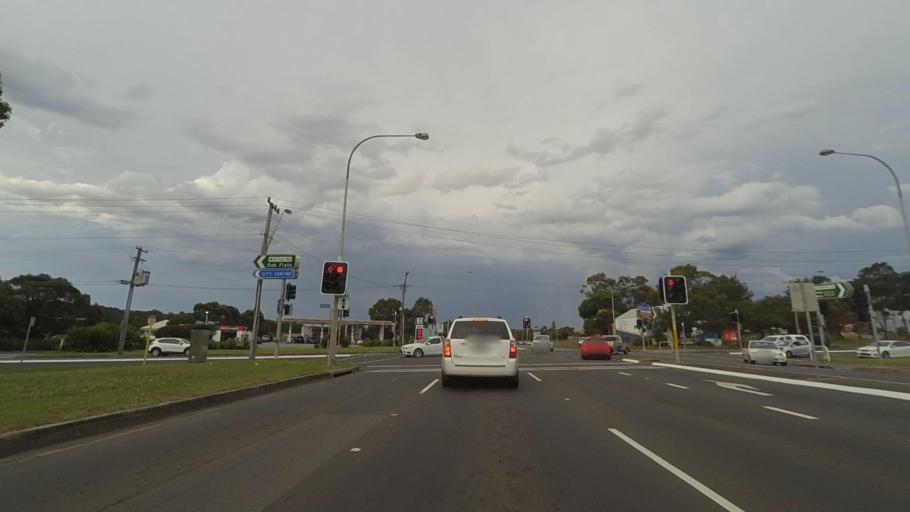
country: AU
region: New South Wales
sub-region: Shellharbour
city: Flinders
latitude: -34.5813
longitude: 150.8608
